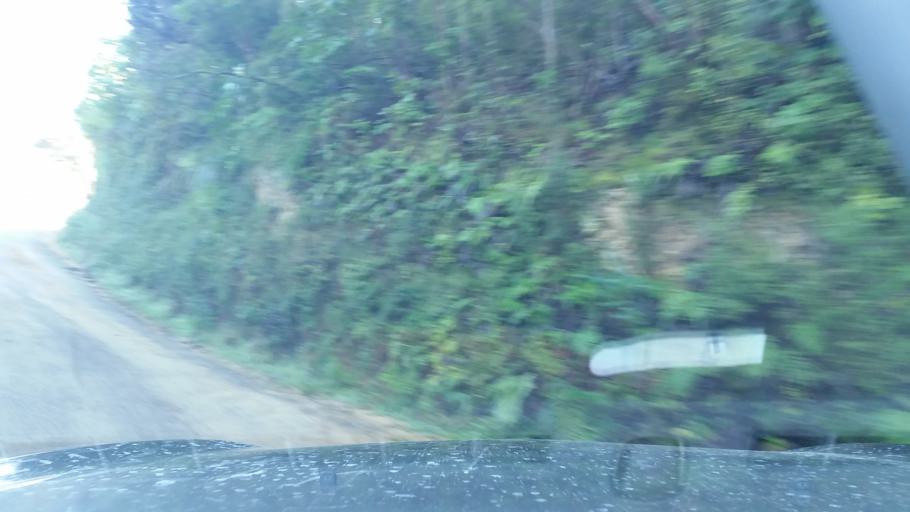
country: NZ
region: Marlborough
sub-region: Marlborough District
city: Picton
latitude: -41.1257
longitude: 173.9918
